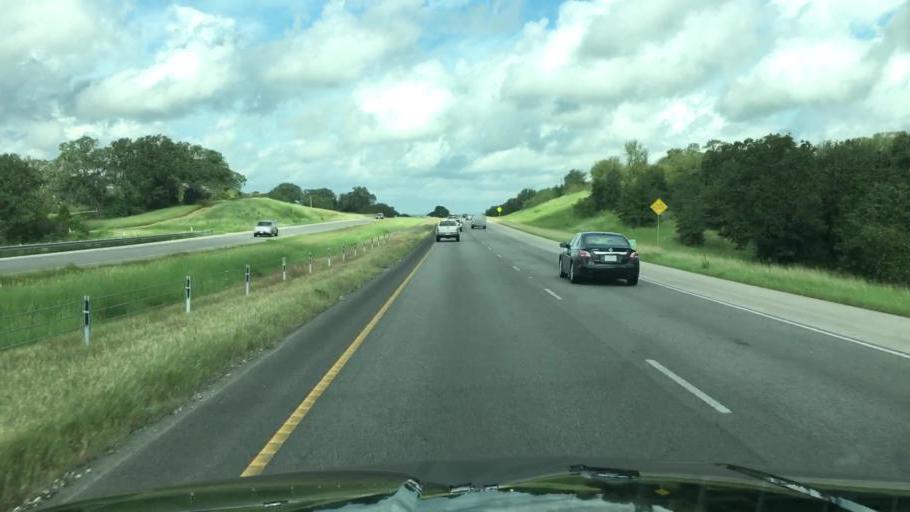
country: US
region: Texas
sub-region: Bastrop County
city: Wyldwood
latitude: 30.1499
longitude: -97.4863
